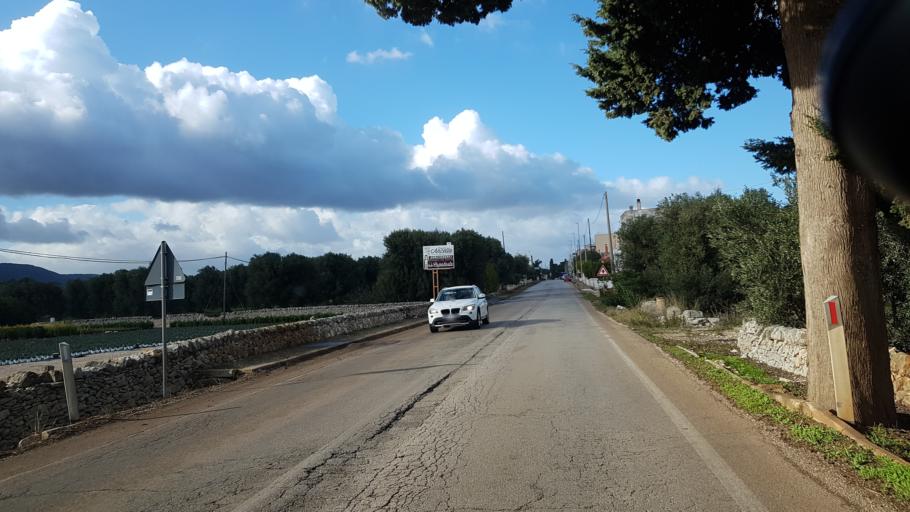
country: IT
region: Apulia
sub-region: Provincia di Brindisi
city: Montalbano
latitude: 40.7899
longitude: 17.4636
